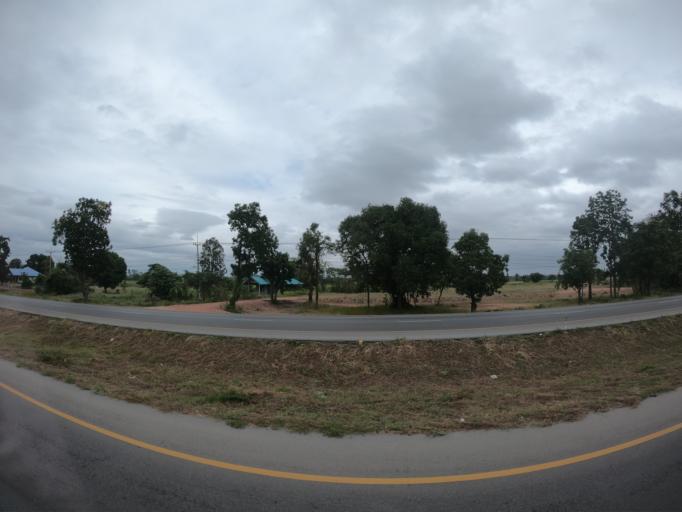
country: TH
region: Khon Kaen
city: Ban Phai
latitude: 16.0443
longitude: 102.8476
